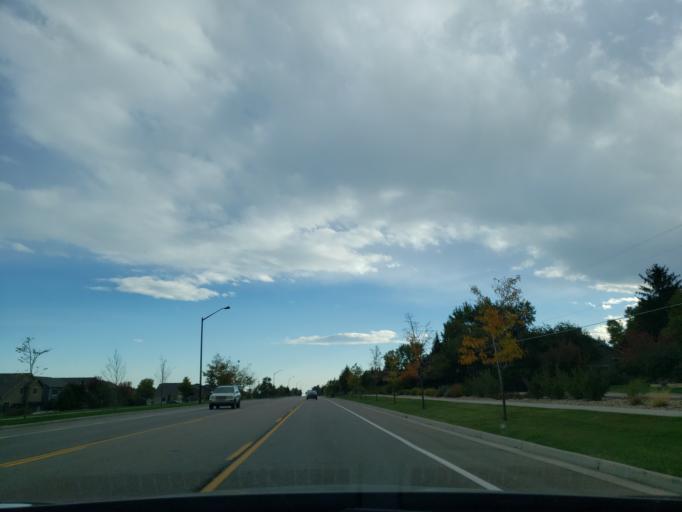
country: US
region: Colorado
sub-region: Larimer County
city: Fort Collins
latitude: 40.6227
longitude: -105.0388
